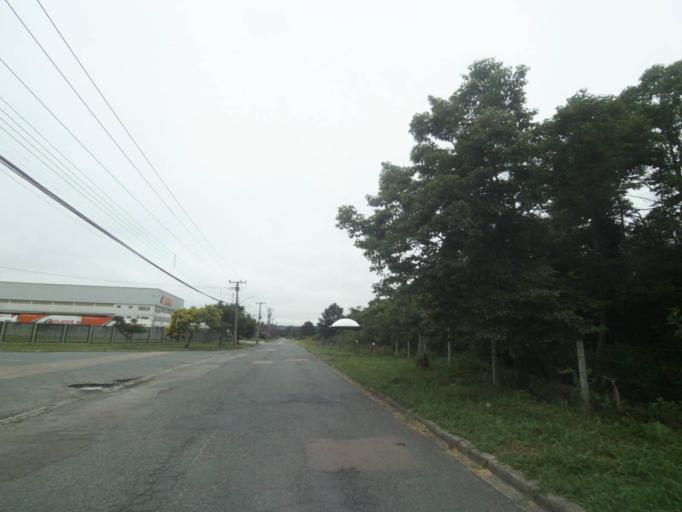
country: BR
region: Parana
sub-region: Araucaria
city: Araucaria
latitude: -25.5382
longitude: -49.3300
